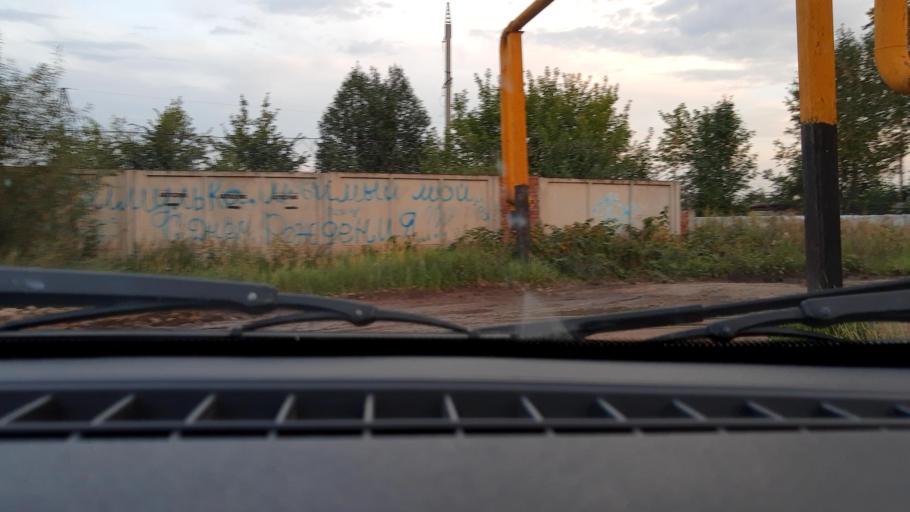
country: RU
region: Bashkortostan
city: Mikhaylovka
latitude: 54.7902
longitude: 55.8621
